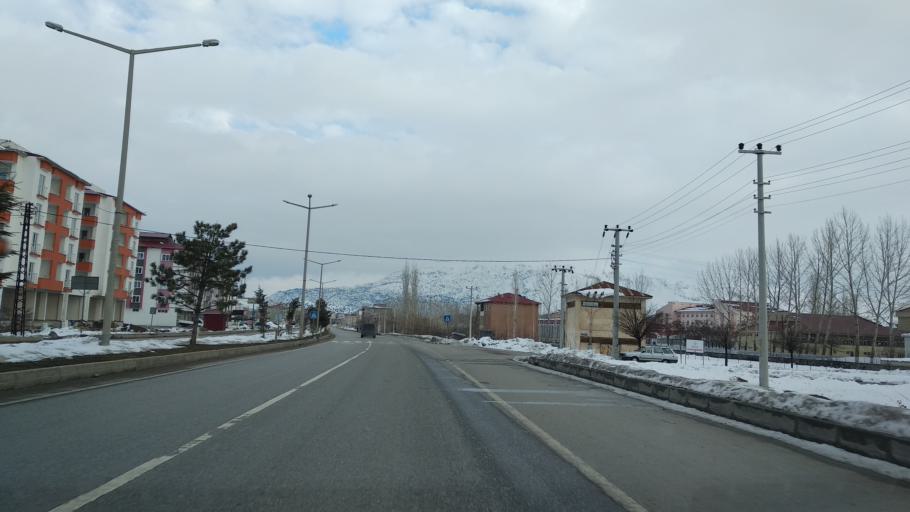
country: TR
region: Kahramanmaras
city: Goksun
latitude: 38.0269
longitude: 36.4864
